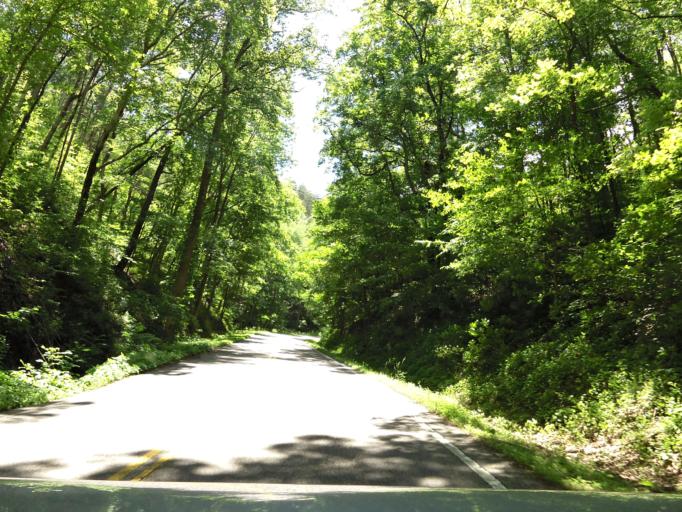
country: US
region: Tennessee
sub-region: Loudon County
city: Greenback
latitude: 35.5165
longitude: -83.9889
